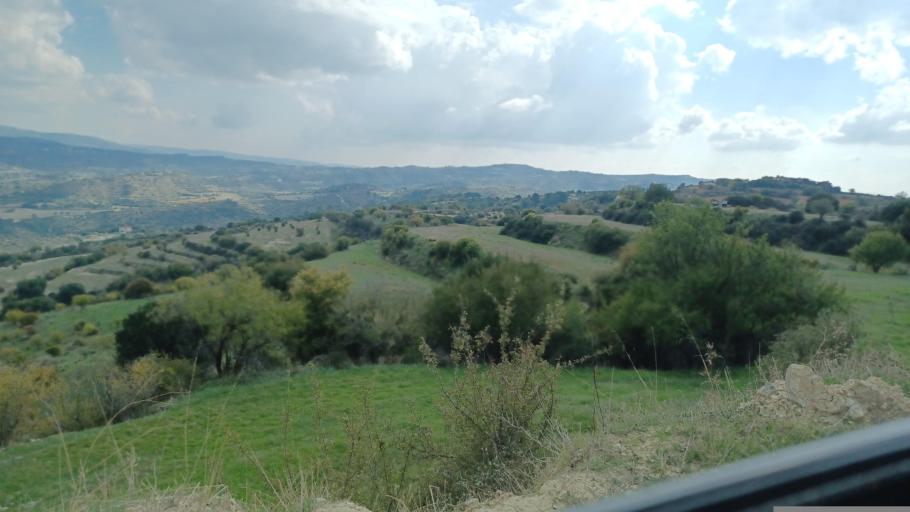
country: CY
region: Pafos
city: Mesogi
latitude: 34.8387
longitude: 32.5254
